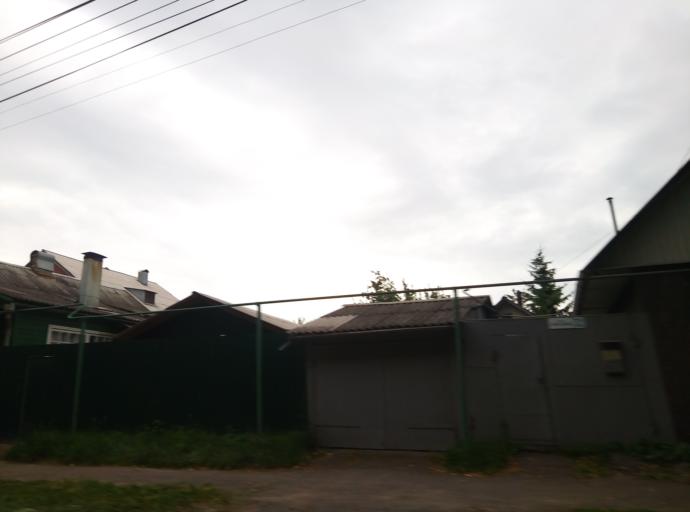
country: RU
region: Kursk
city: Kursk
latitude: 51.7435
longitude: 36.1562
